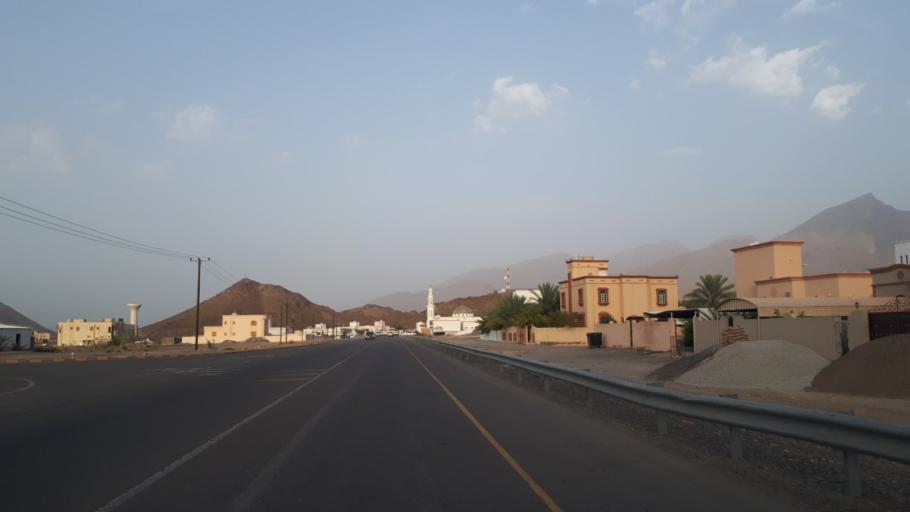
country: OM
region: Al Batinah
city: Rustaq
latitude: 23.3863
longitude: 57.1922
